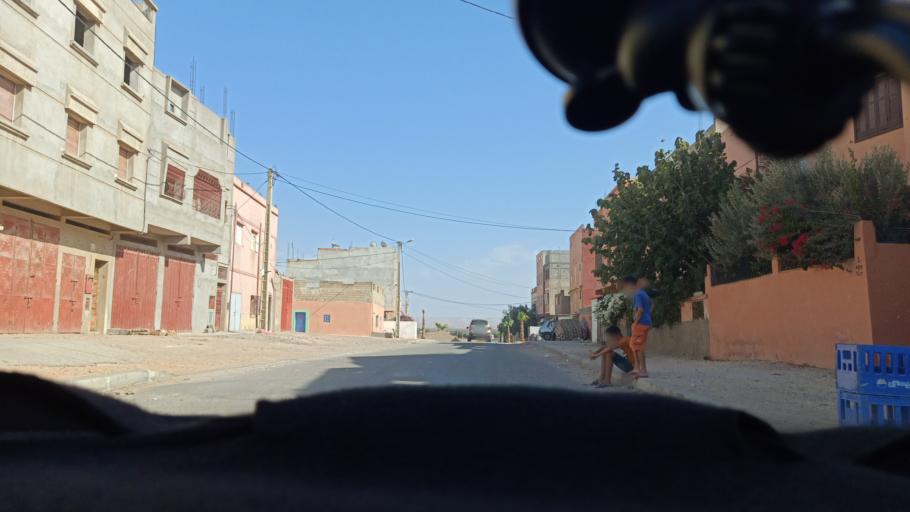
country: MA
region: Doukkala-Abda
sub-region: Safi
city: Youssoufia
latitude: 32.3519
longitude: -8.8370
